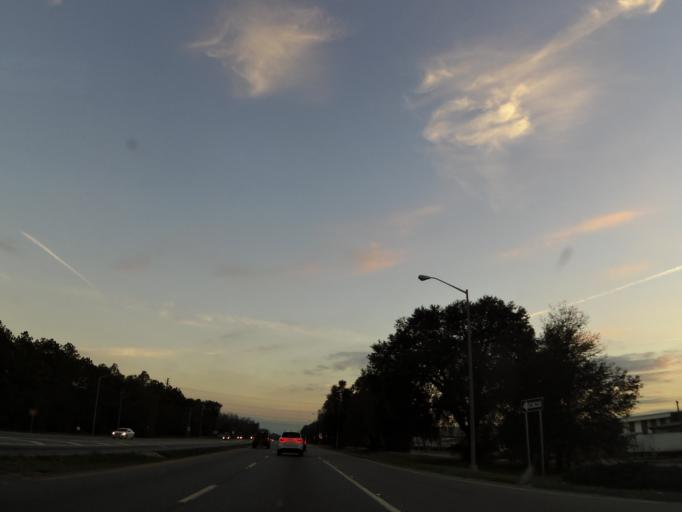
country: US
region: Georgia
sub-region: Dougherty County
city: Albany
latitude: 31.5560
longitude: -84.1152
